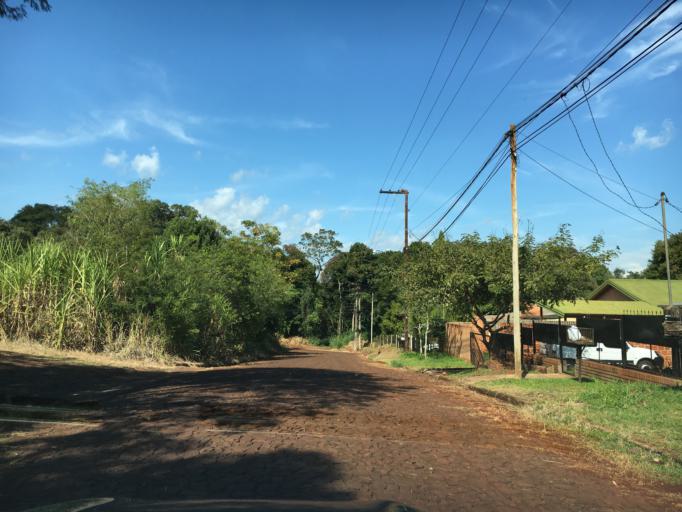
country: AR
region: Misiones
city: Puerto Rico
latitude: -26.8194
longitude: -55.0361
